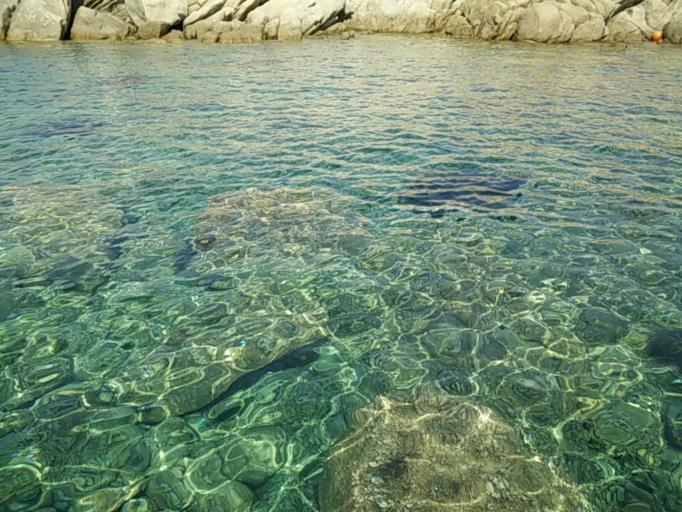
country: FR
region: Corsica
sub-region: Departement de la Corse-du-Sud
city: Propriano
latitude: 41.5666
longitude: 8.7898
